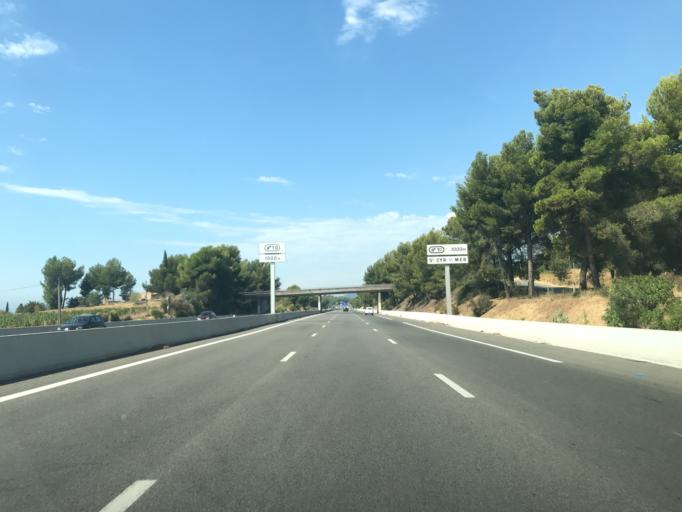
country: FR
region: Provence-Alpes-Cote d'Azur
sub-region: Departement du Var
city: Saint-Cyr-sur-Mer
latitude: 43.1966
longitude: 5.7039
